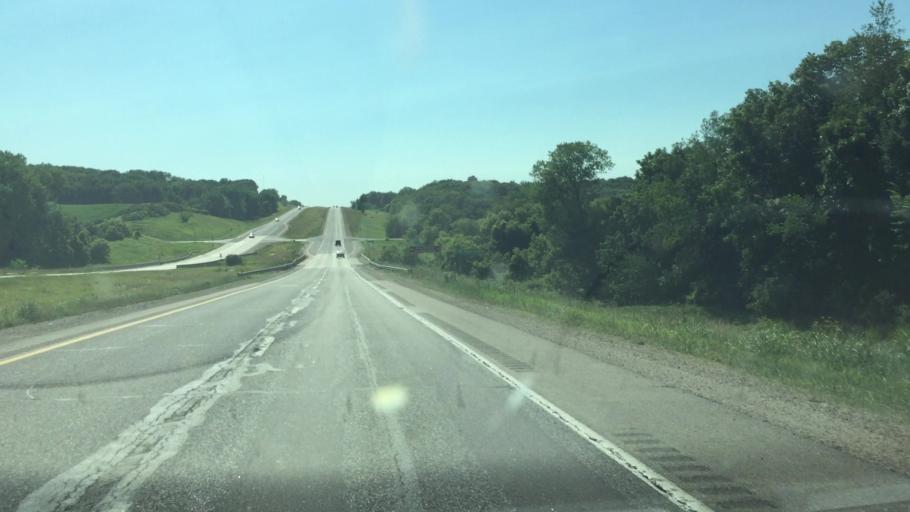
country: US
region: Iowa
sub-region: Linn County
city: Ely
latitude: 41.9254
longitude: -91.5748
